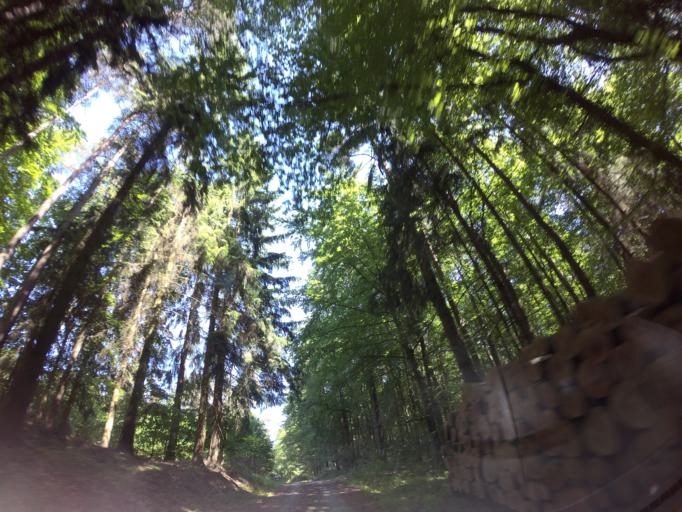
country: PL
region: West Pomeranian Voivodeship
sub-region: Powiat choszczenski
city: Recz
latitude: 53.3147
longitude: 15.6034
